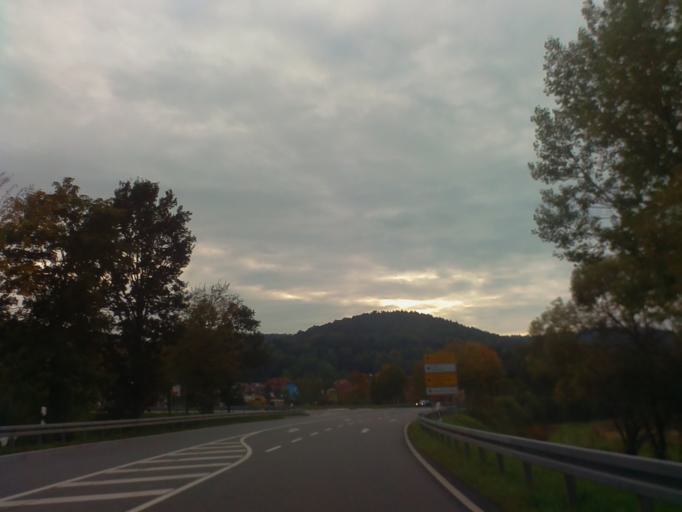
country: DE
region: Hesse
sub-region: Regierungsbezirk Darmstadt
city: Lutzelbach
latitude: 49.8160
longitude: 9.0457
